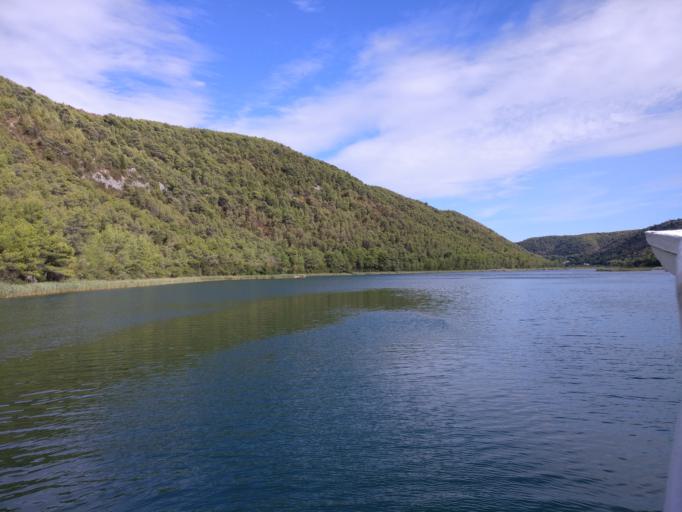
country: HR
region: Sibensko-Kniniska
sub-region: Grad Sibenik
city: Sibenik
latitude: 43.8215
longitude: 15.9446
